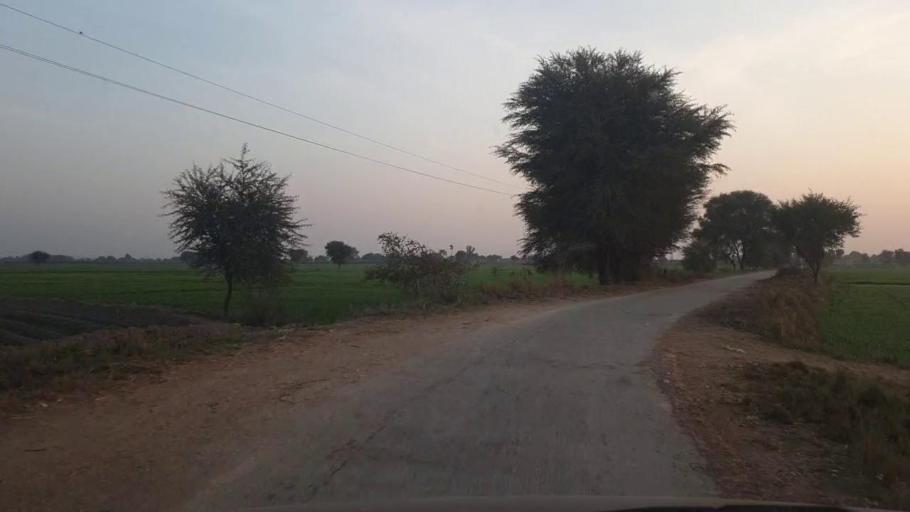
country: PK
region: Sindh
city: Bhit Shah
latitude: 25.8564
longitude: 68.5145
